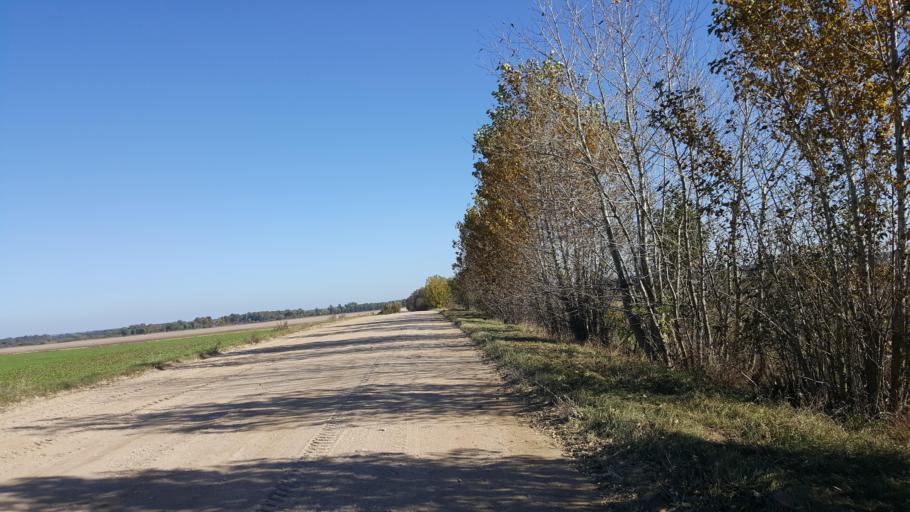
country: BY
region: Brest
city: Kamyanyets
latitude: 52.4128
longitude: 23.8569
